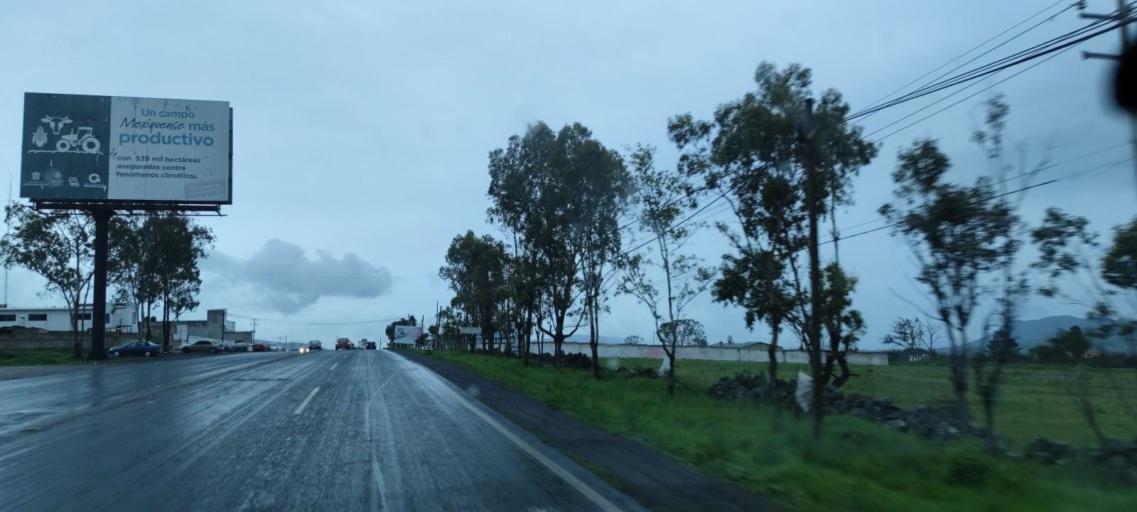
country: MX
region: Mexico
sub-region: Jilotepec
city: Jilotepec de Molina Enriquez
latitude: 19.9503
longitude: -99.5506
